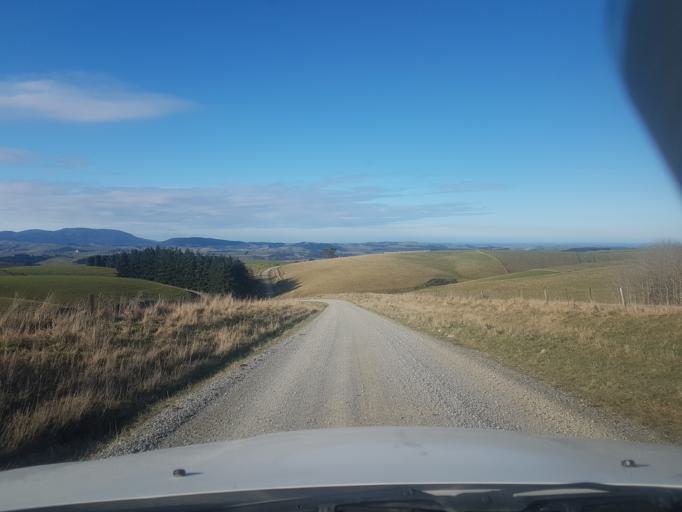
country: NZ
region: Canterbury
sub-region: Timaru District
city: Pleasant Point
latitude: -44.1675
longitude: 170.9084
